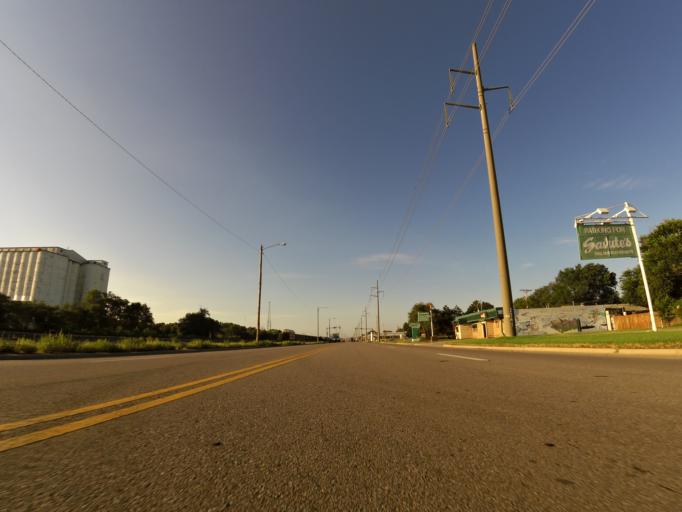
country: US
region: Kansas
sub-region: Sedgwick County
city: Wichita
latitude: 37.7440
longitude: -97.3360
